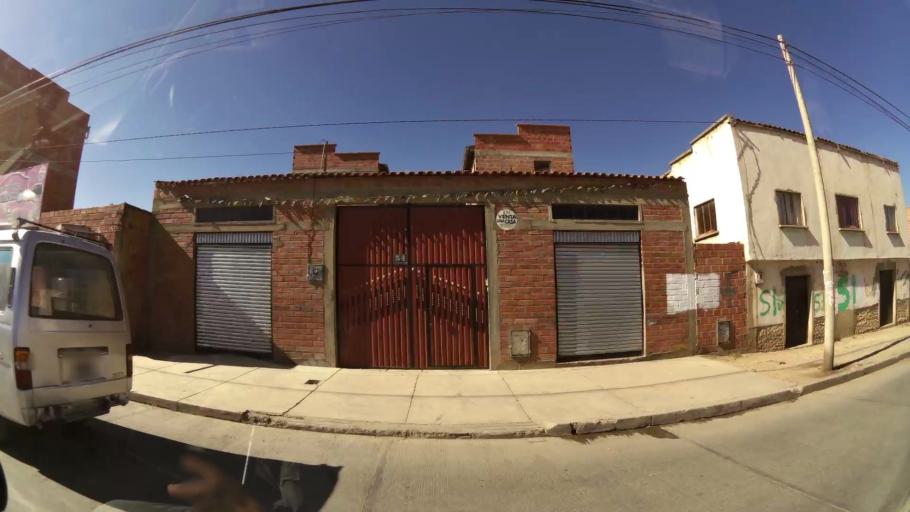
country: BO
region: La Paz
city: La Paz
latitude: -16.5272
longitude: -68.2041
